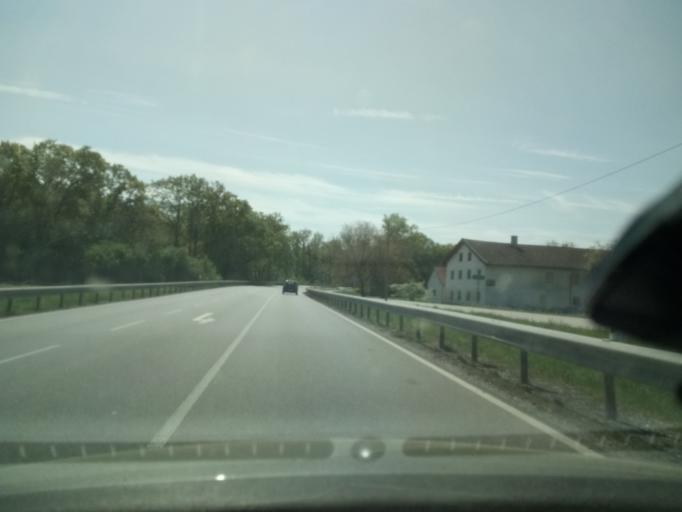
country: DE
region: Bavaria
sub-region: Upper Bavaria
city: Ampfing
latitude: 48.2340
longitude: 12.4138
